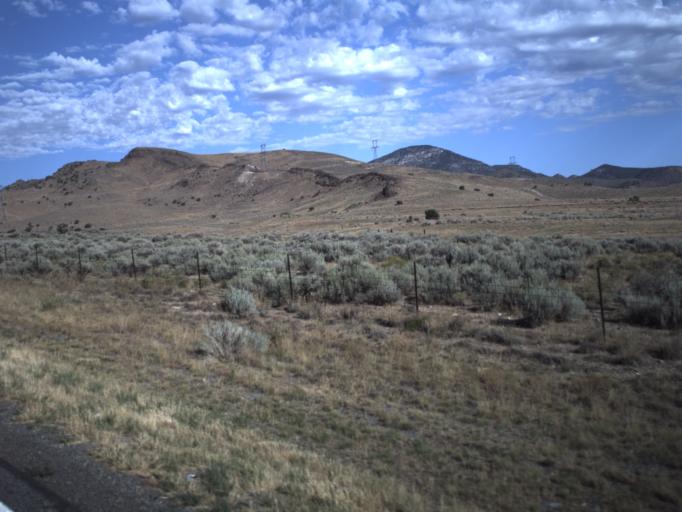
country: US
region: Utah
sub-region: Utah County
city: Genola
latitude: 39.9513
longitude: -111.9967
